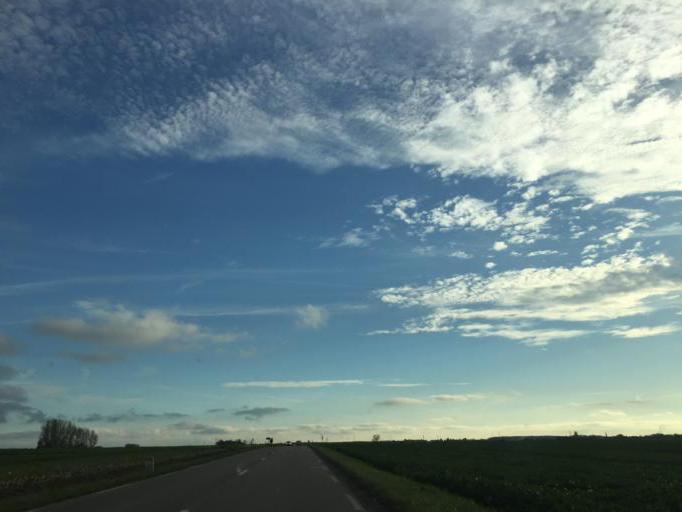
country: FR
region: Ile-de-France
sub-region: Departement de Seine-et-Marne
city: Jouy-le-Chatel
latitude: 48.6401
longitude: 3.1028
